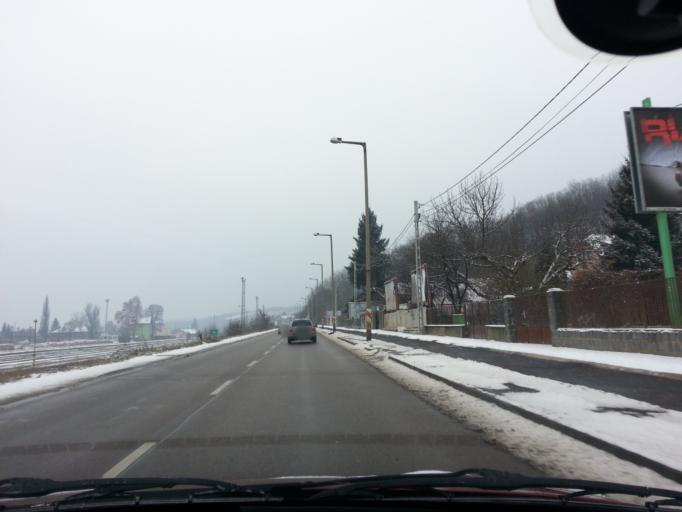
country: HU
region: Nograd
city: Salgotarjan
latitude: 48.0932
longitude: 19.7936
